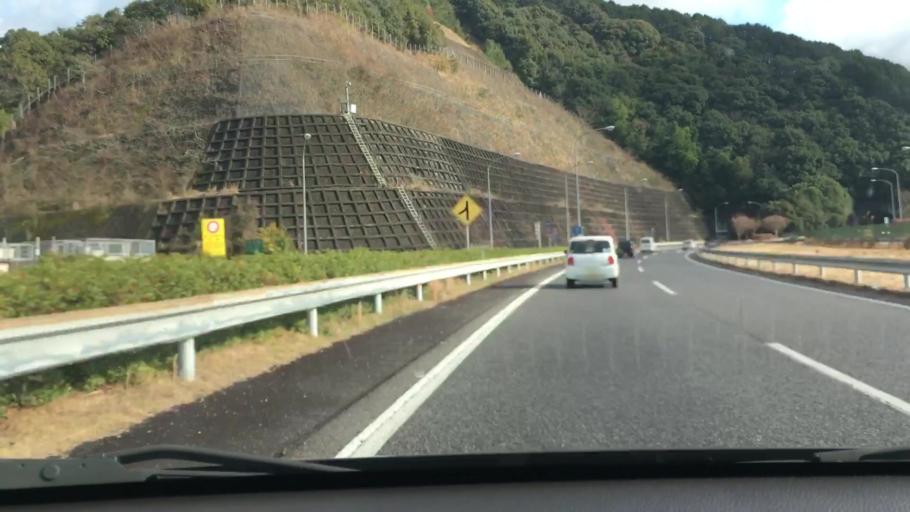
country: JP
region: Kumamoto
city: Yatsushiro
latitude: 32.4423
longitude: 130.6692
